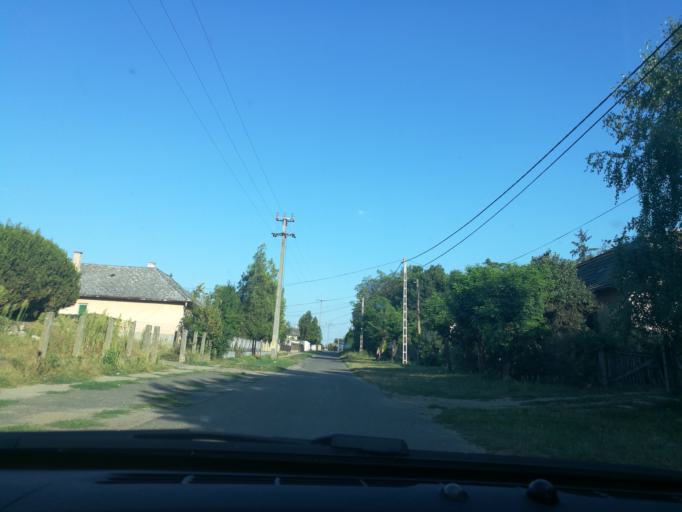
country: HU
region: Szabolcs-Szatmar-Bereg
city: Tiszabercel
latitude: 48.1640
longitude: 21.5927
